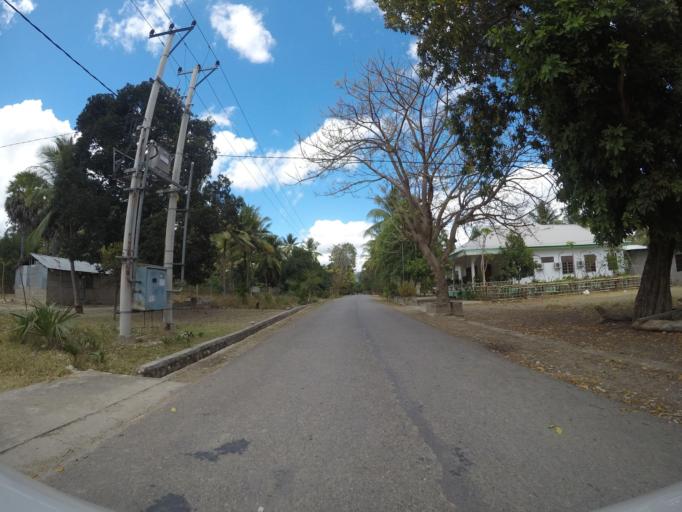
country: TL
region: Lautem
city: Lospalos
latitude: -8.4505
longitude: 126.8234
